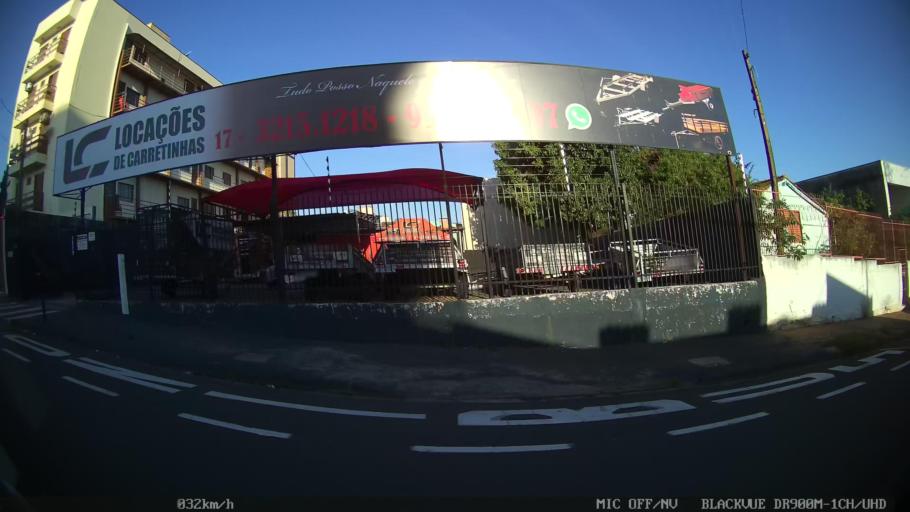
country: BR
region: Sao Paulo
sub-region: Sao Jose Do Rio Preto
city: Sao Jose do Rio Preto
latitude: -20.8053
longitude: -49.3719
